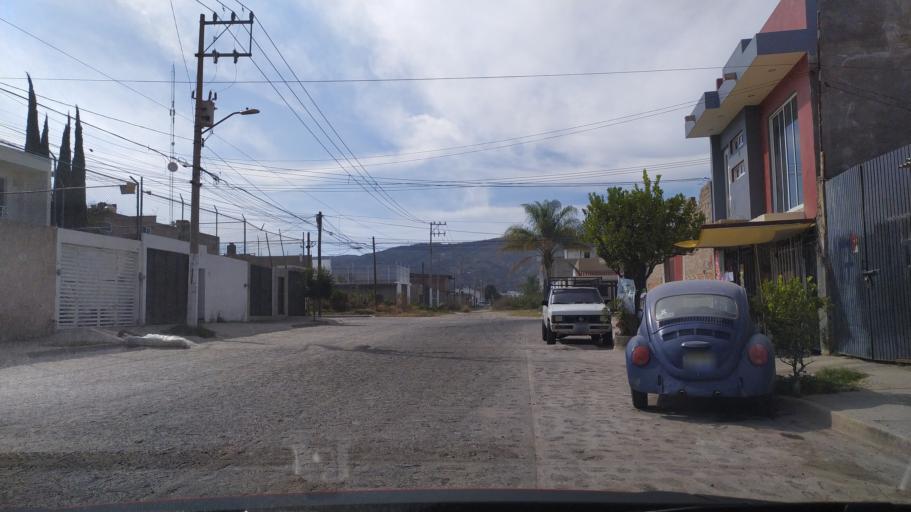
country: MX
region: Jalisco
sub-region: Tlajomulco de Zuniga
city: Palomar
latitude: 20.6287
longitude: -103.4735
